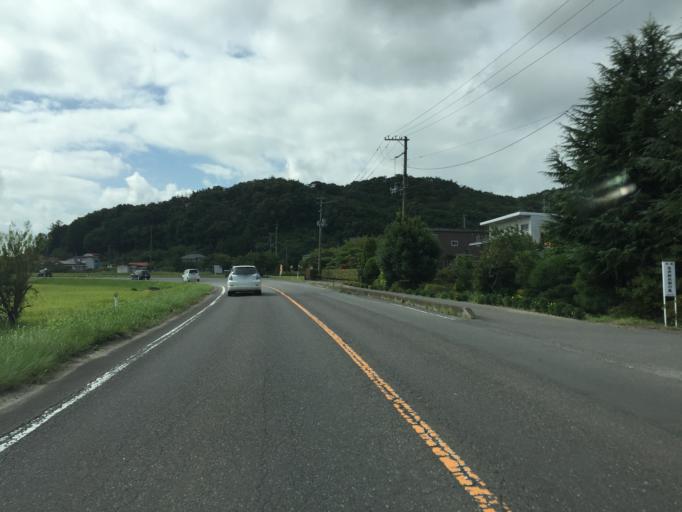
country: JP
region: Fukushima
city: Motomiya
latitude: 37.4909
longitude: 140.3711
